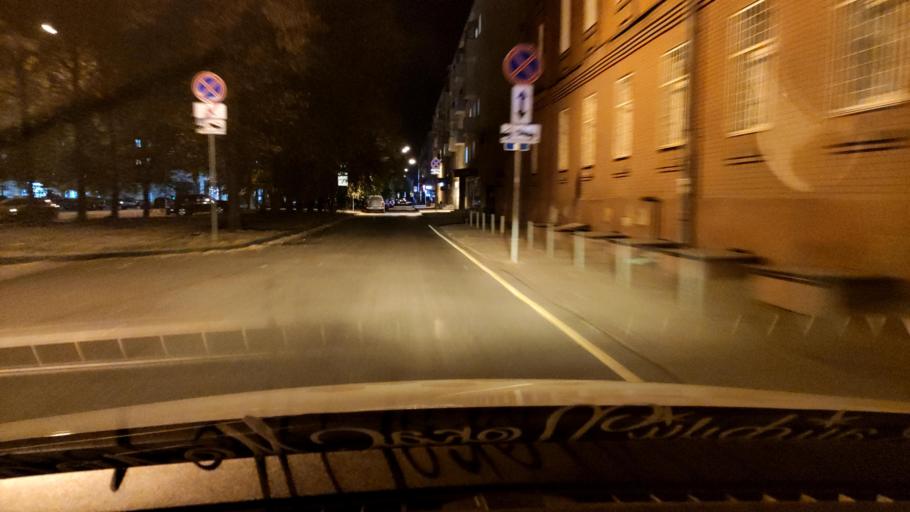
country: RU
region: Voronezj
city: Voronezh
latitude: 51.6555
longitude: 39.1906
